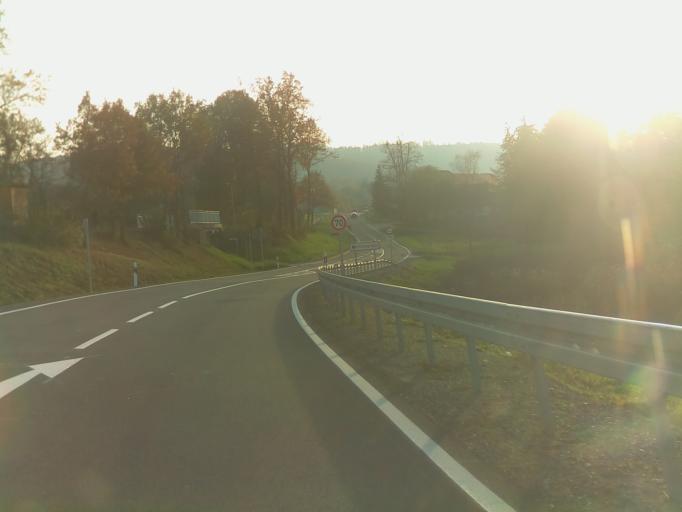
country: DE
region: Bavaria
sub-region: Regierungsbezirk Unterfranken
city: Zeitlofs
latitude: 50.2747
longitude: 9.7142
